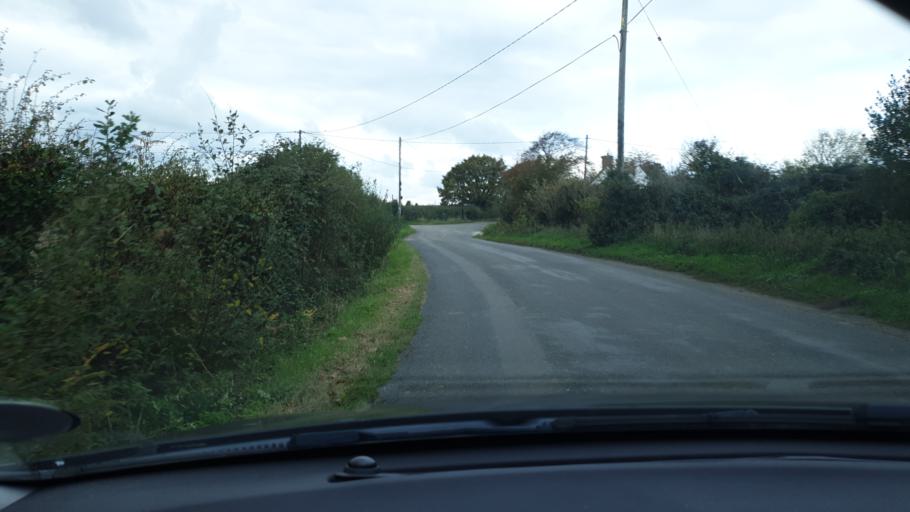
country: GB
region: England
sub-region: Essex
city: Mistley
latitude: 51.9316
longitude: 1.0985
